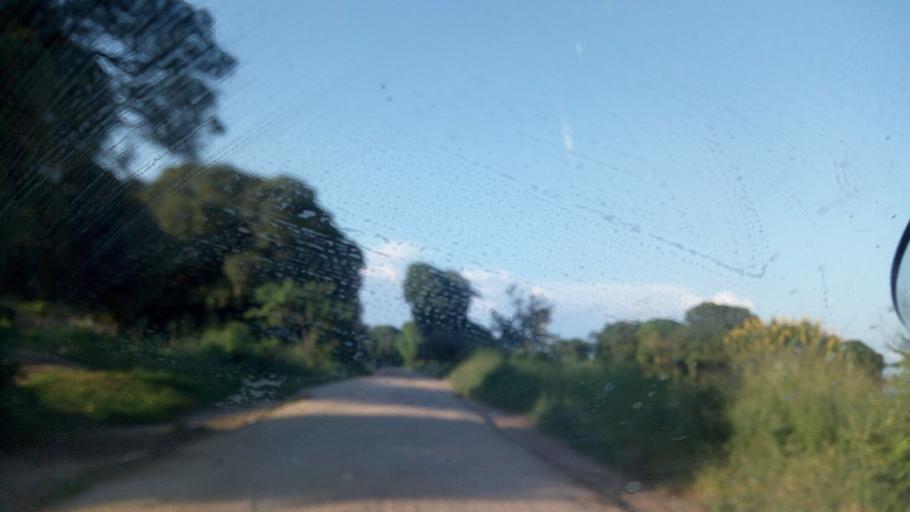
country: BI
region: Bururi
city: Rumonge
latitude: -4.1237
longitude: 29.0828
